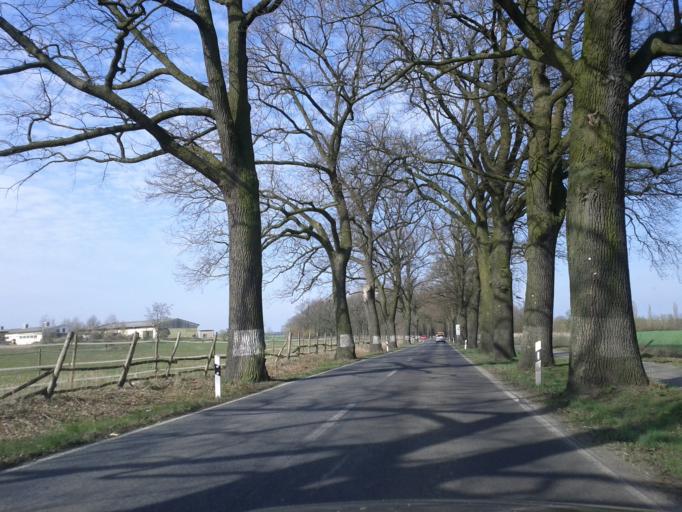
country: DE
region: Brandenburg
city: Schoneiche
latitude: 52.4830
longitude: 13.6941
